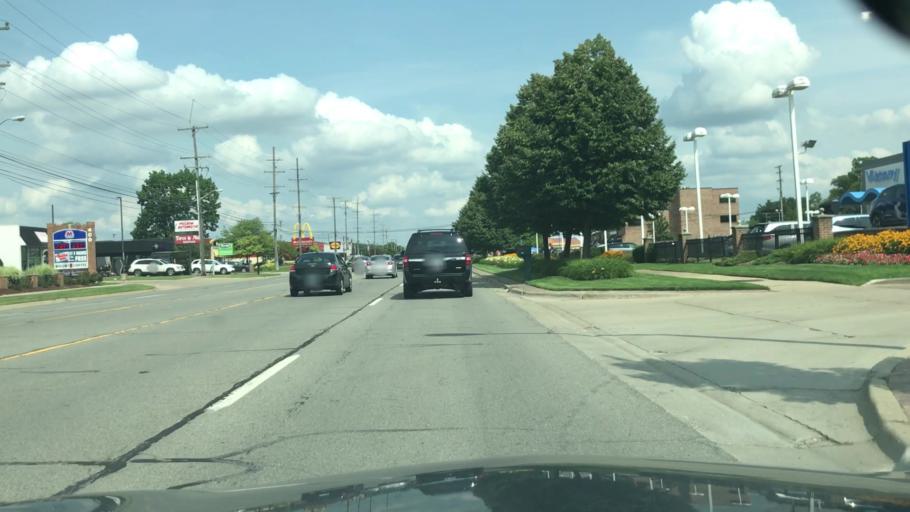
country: US
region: Michigan
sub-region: Wayne County
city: Plymouth
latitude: 42.3588
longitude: -83.4644
